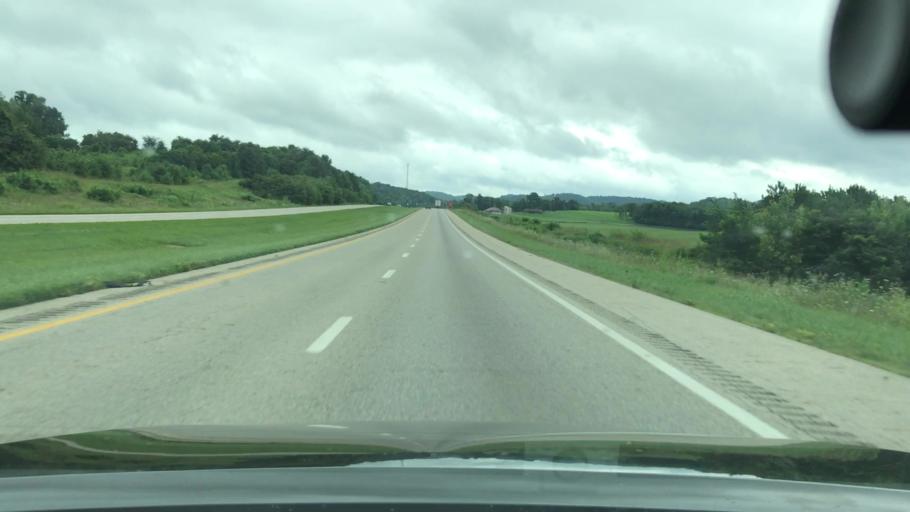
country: US
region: Ohio
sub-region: Ross County
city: Chillicothe
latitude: 39.2625
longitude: -82.8669
